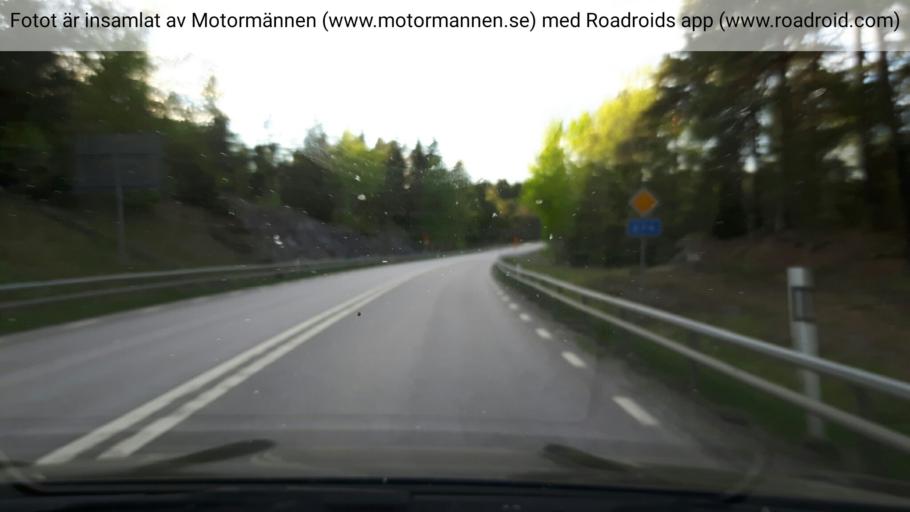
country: SE
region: Stockholm
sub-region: Lidingo
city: Brevik
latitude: 59.4299
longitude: 18.2209
